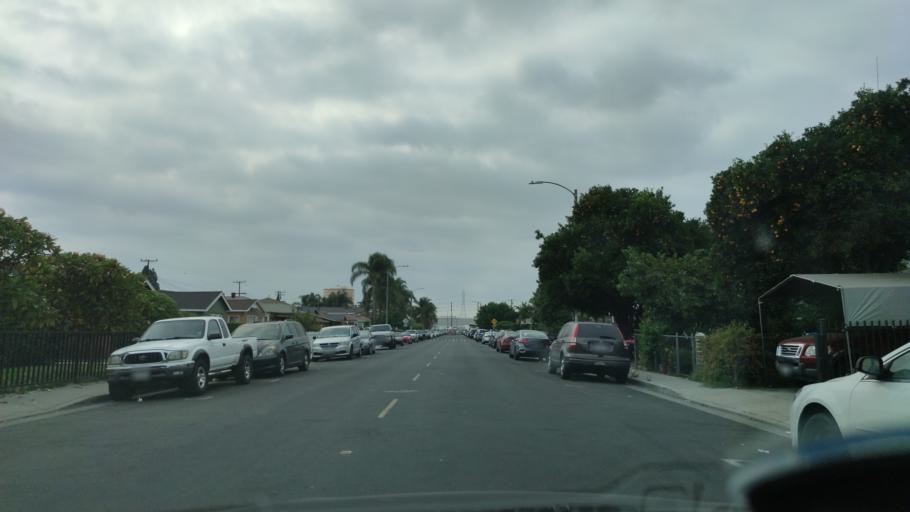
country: US
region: California
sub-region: Los Angeles County
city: Maywood
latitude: 33.9955
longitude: -118.2006
